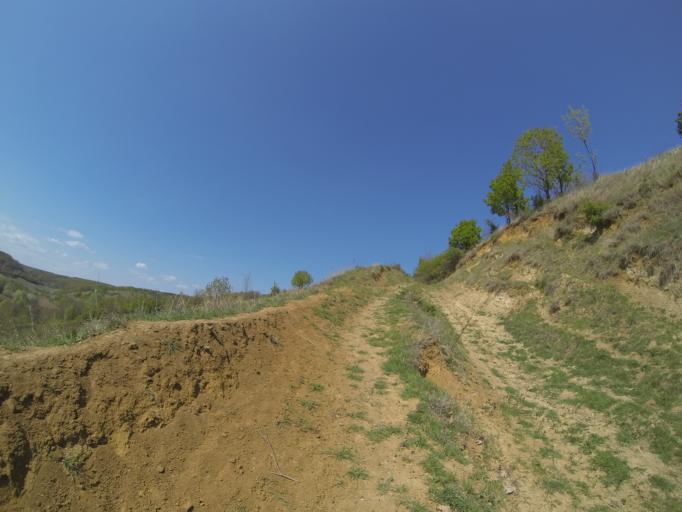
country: RO
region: Gorj
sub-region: Comuna Crusetu
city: Crusetu
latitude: 44.6063
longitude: 23.6507
